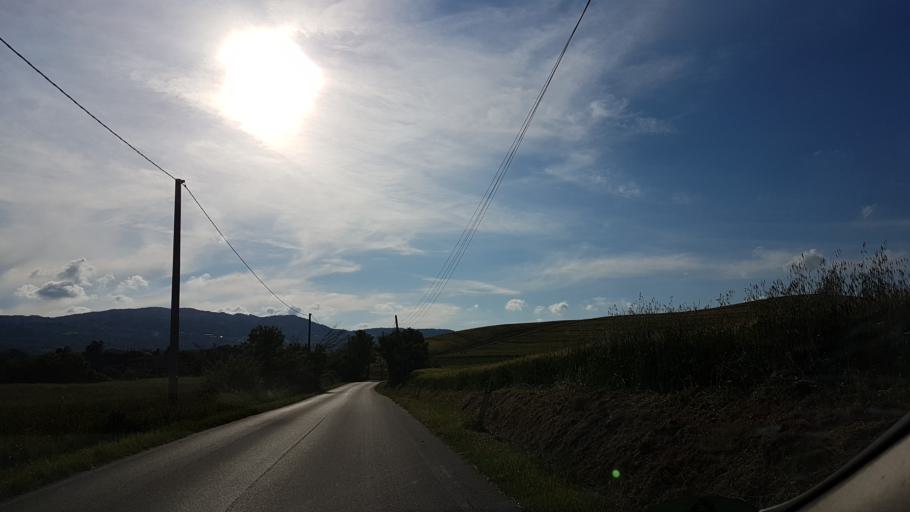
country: IT
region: Tuscany
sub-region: Province of Pisa
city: Lajatico
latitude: 43.4814
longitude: 10.6875
